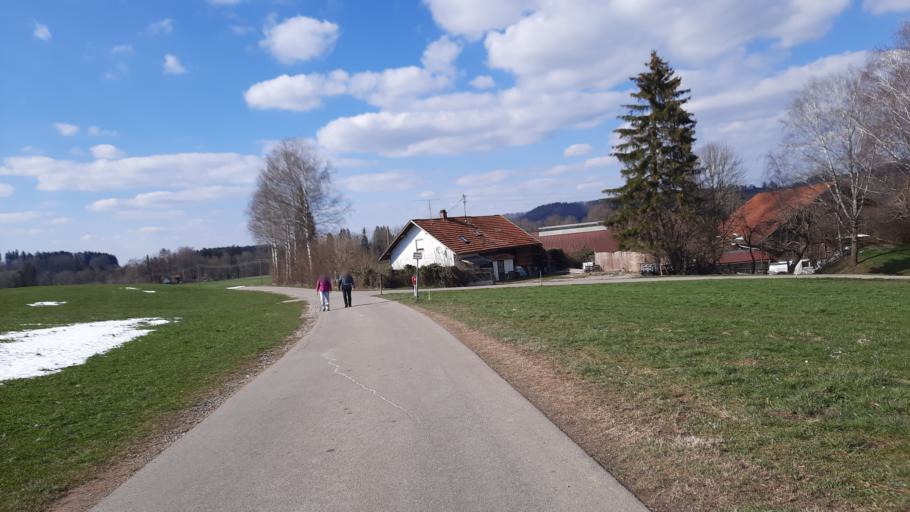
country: DE
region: Bavaria
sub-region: Swabia
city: Altusried
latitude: 47.8189
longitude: 10.2028
